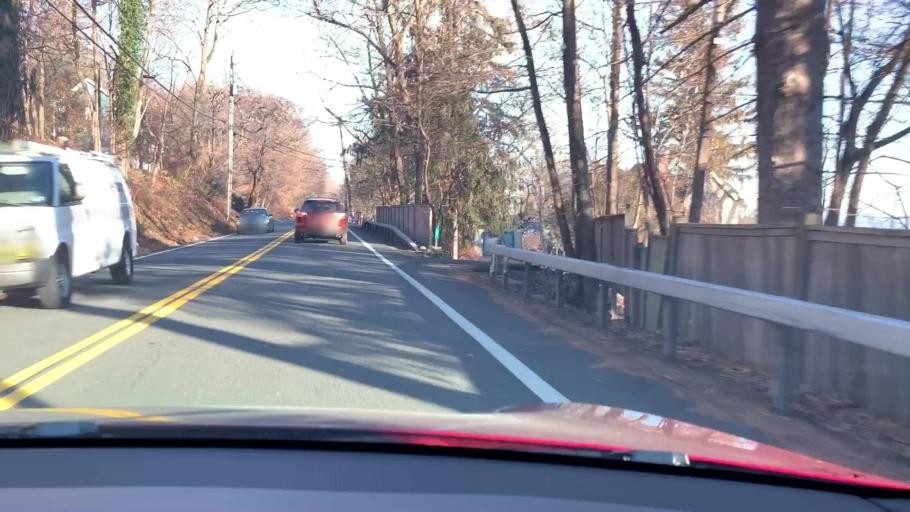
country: US
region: New York
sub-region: Rockland County
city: Piermont
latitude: 41.0444
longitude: -73.9211
